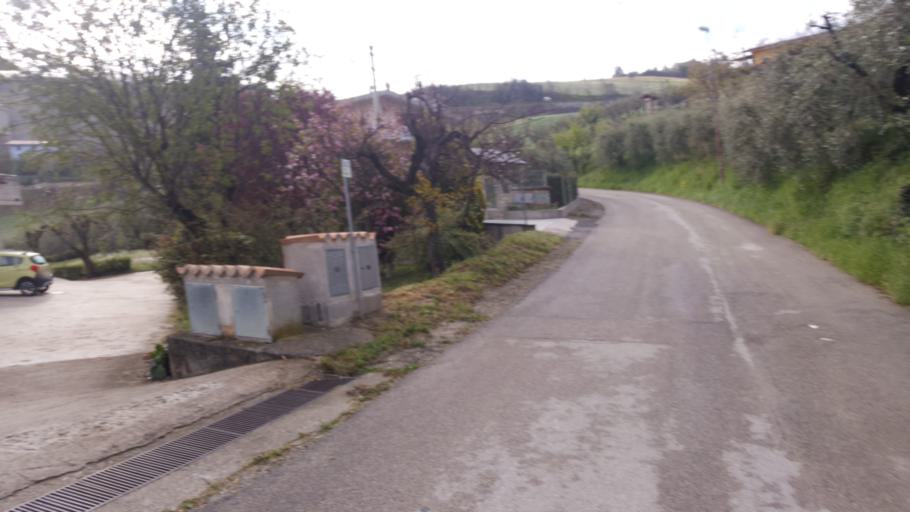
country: IT
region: The Marches
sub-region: Provincia di Ascoli Piceno
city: Venarotta
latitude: 42.8682
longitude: 13.5329
